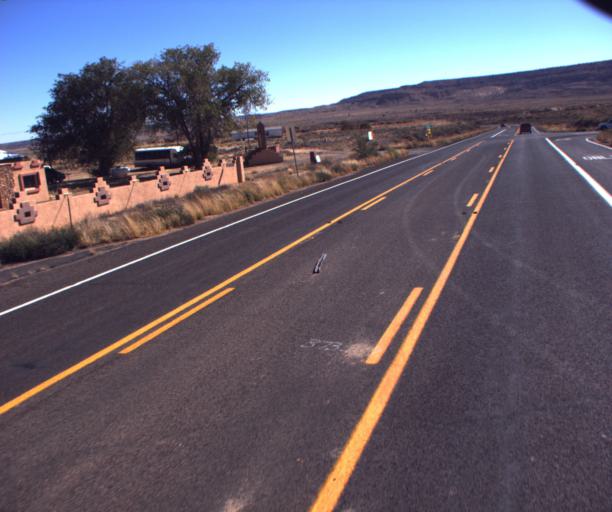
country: US
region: Arizona
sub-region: Navajo County
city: First Mesa
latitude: 35.8761
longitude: -110.6075
